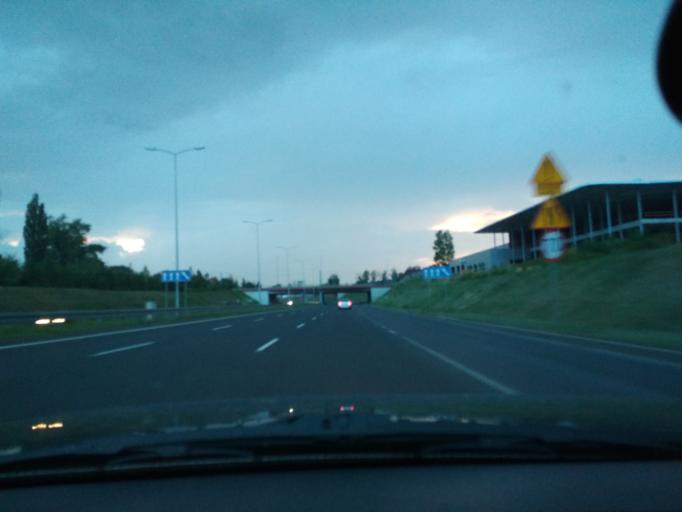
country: PL
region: Silesian Voivodeship
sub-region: Swietochlowice
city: Swietochlowice
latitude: 50.2983
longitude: 18.8831
